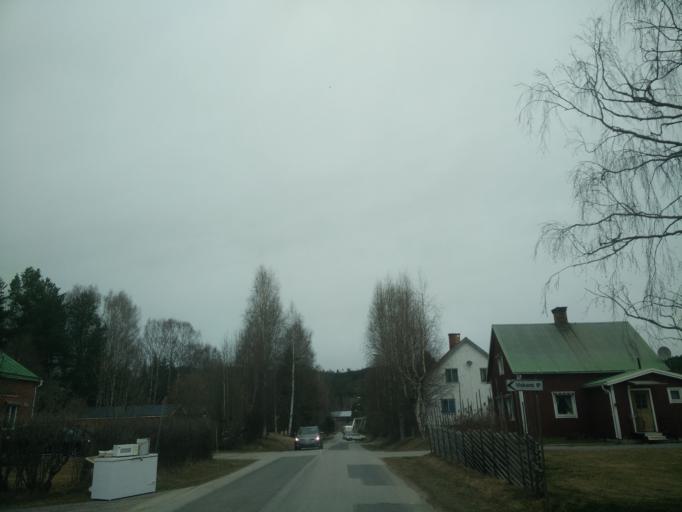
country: SE
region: Vaesternorrland
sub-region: Ange Kommun
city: Fransta
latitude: 62.4459
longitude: 16.4319
